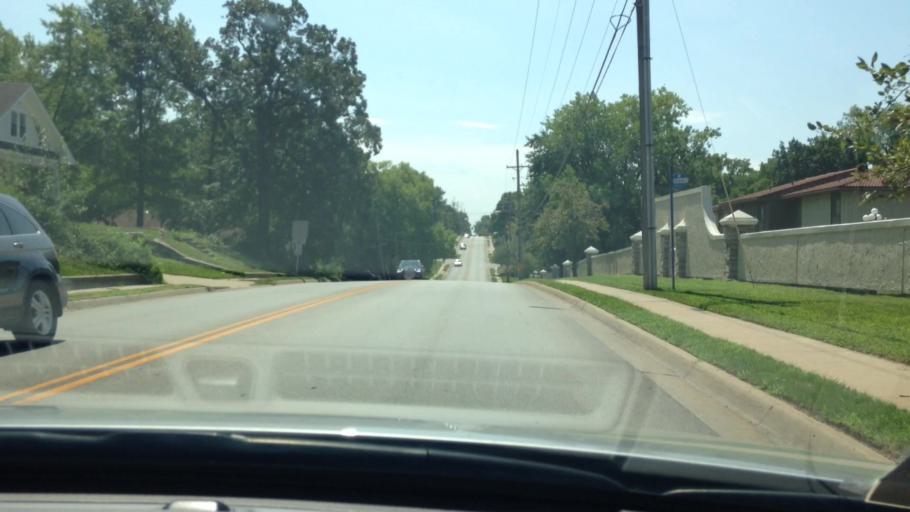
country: US
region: Kansas
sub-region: Johnson County
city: Westwood
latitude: 39.0492
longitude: -94.6213
